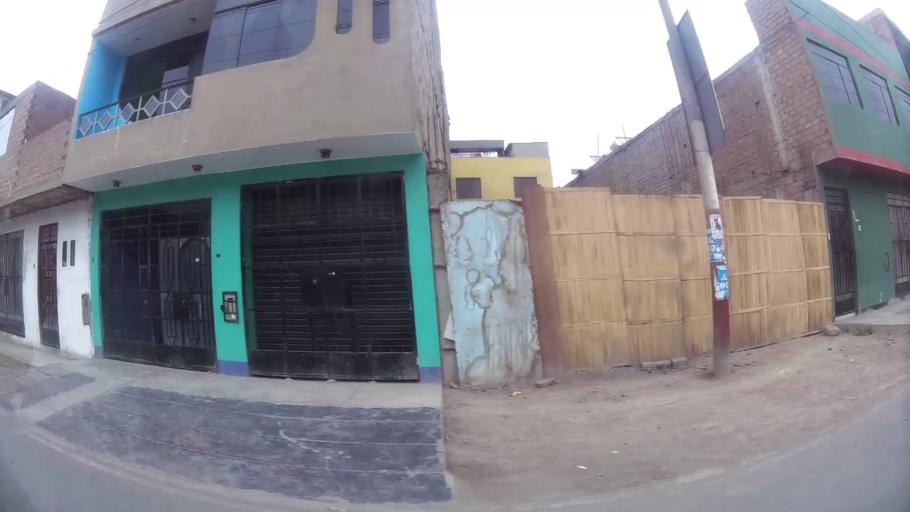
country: PE
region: Lima
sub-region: Lima
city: Independencia
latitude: -11.9494
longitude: -77.0874
